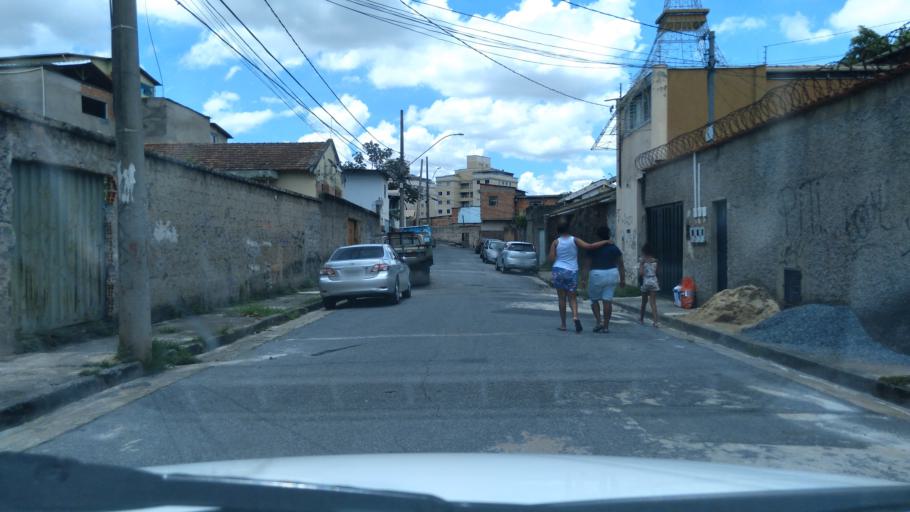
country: BR
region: Minas Gerais
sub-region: Belo Horizonte
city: Belo Horizonte
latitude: -19.9191
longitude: -43.9084
